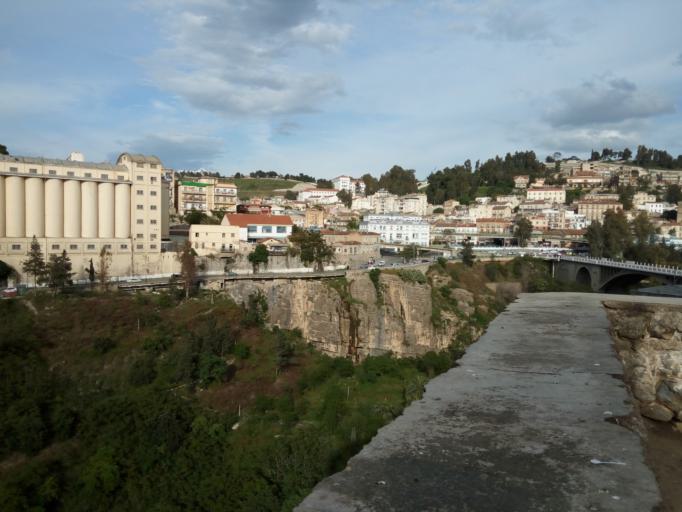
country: DZ
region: Constantine
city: Constantine
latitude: 36.3699
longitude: 6.6162
